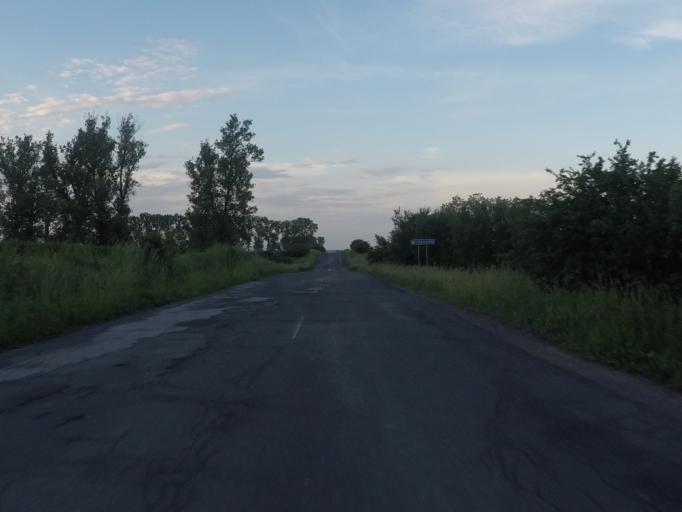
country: SK
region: Banskobystricky
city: Fil'akovo
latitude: 48.3321
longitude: 19.8190
